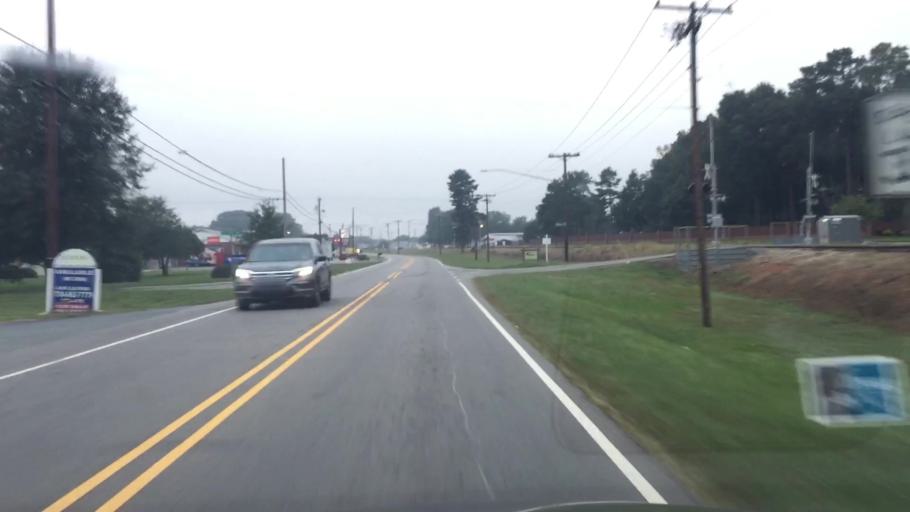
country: US
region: North Carolina
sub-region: Iredell County
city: Mooresville
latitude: 35.5971
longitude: -80.8085
